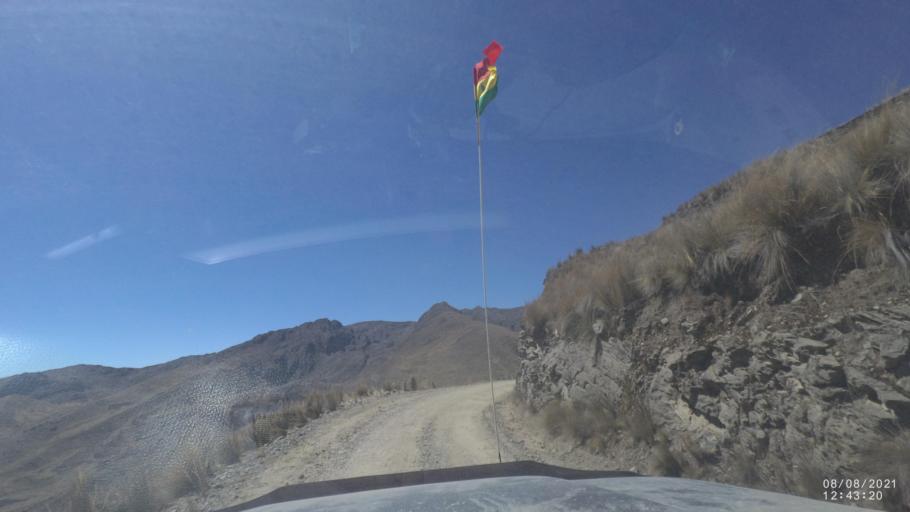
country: BO
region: Cochabamba
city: Colchani
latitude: -16.8429
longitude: -66.6132
